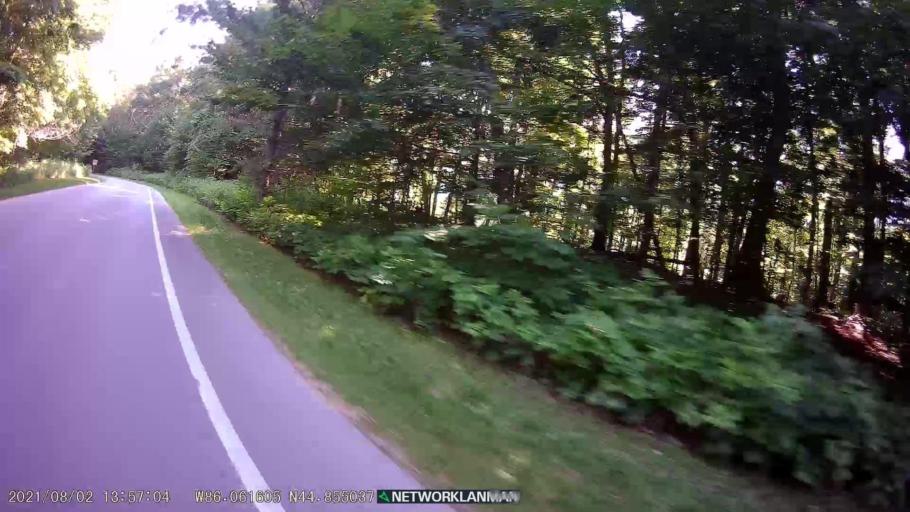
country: US
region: Michigan
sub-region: Benzie County
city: Beulah
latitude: 44.8552
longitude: -86.0617
